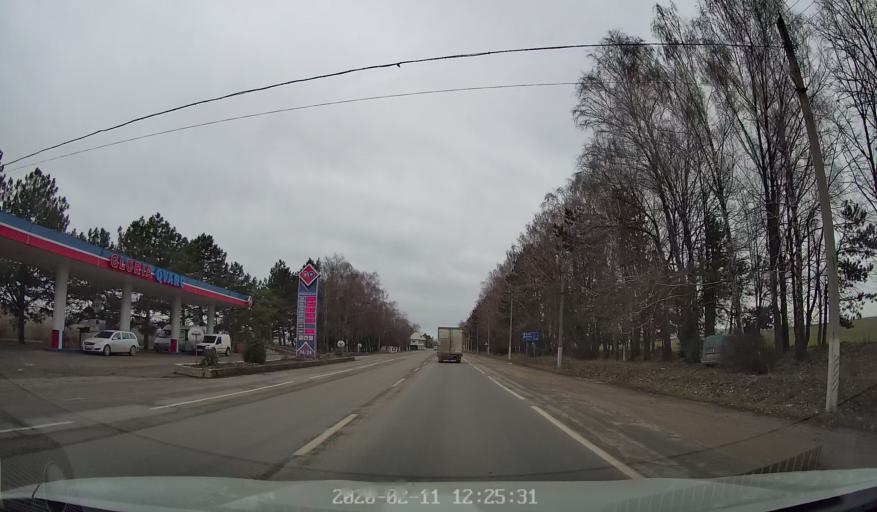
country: MD
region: Raionul Edinet
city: Edinet
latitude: 48.1554
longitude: 27.3351
